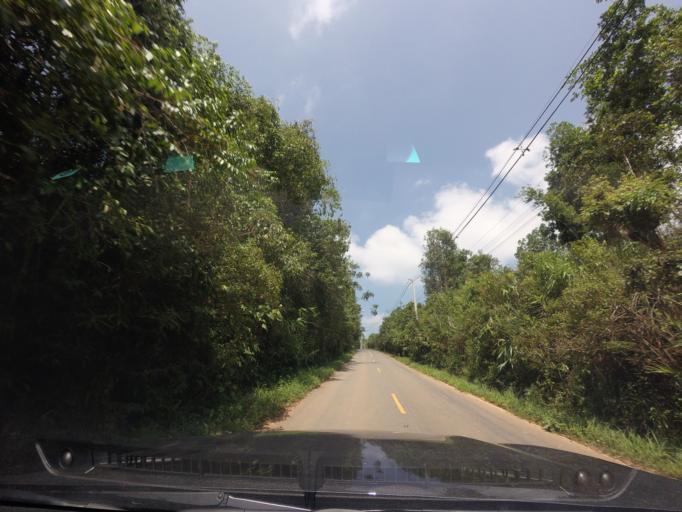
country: TH
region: Loei
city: Na Haeo
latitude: 17.4690
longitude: 100.9224
